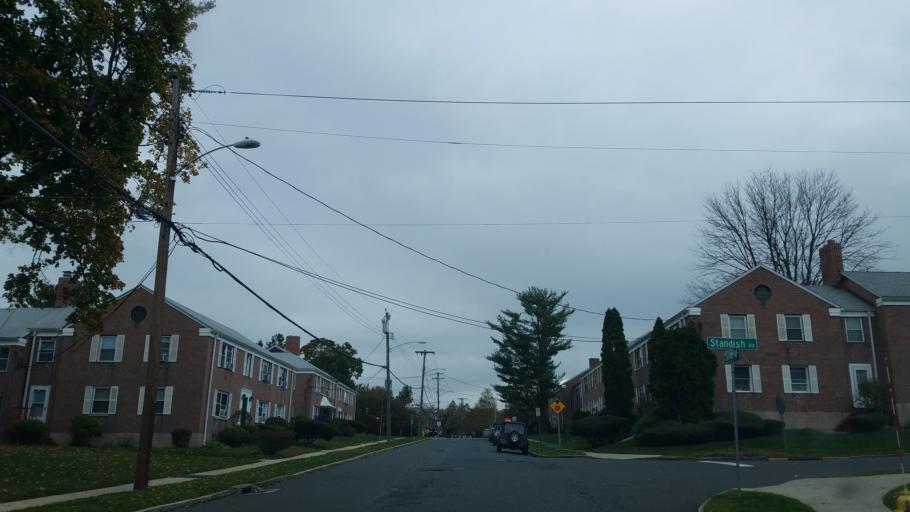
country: US
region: Connecticut
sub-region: Fairfield County
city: Stamford
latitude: 41.0582
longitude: -73.5182
